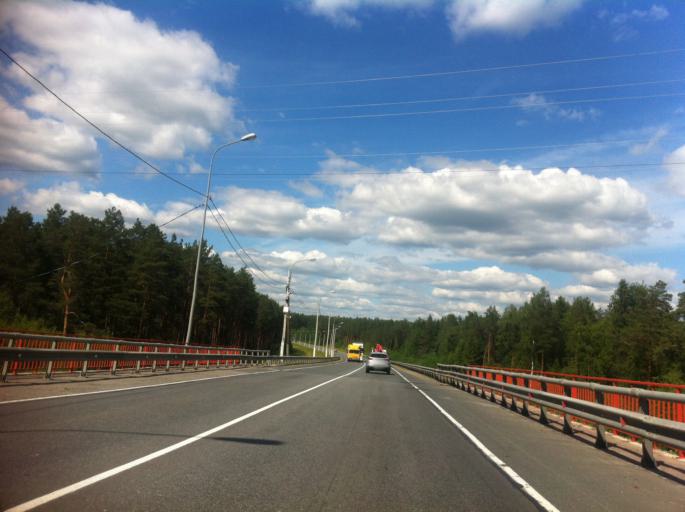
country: RU
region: Leningrad
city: Luga
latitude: 58.7010
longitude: 29.8805
